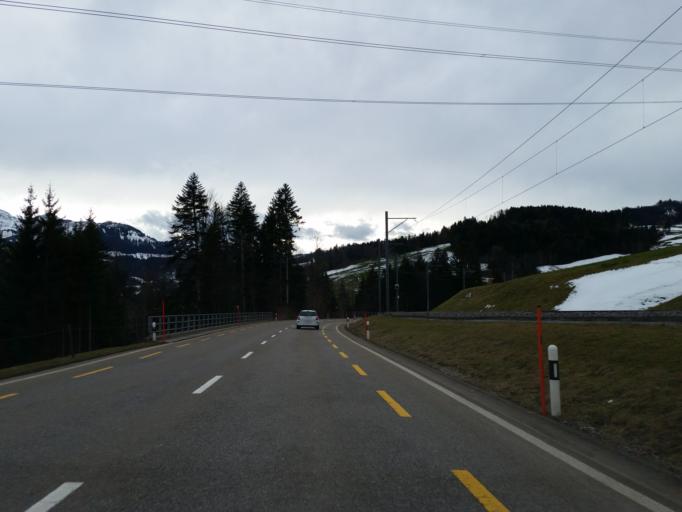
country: CH
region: Appenzell Ausserrhoden
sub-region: Bezirk Hinterland
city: Waldstatt
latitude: 47.3486
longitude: 9.2916
